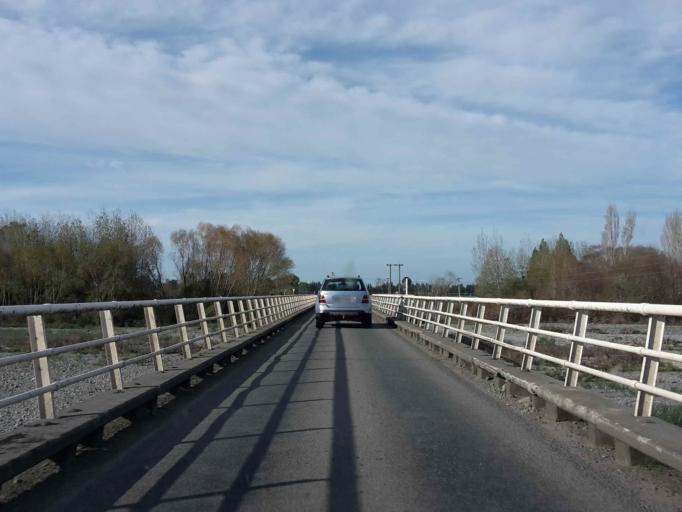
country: NZ
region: Canterbury
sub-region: Timaru District
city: Pleasant Point
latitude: -44.0447
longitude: 171.2685
